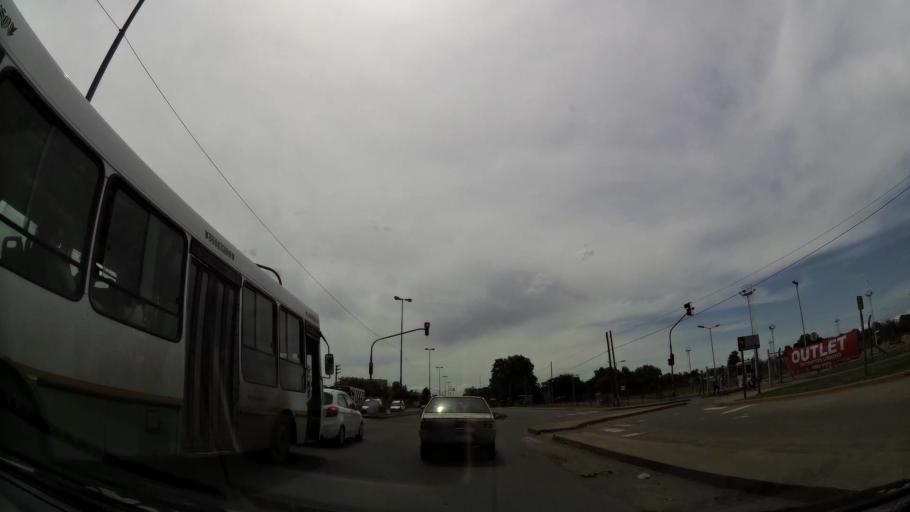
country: AR
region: Buenos Aires
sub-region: Partido de Quilmes
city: Quilmes
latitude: -34.7796
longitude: -58.2795
